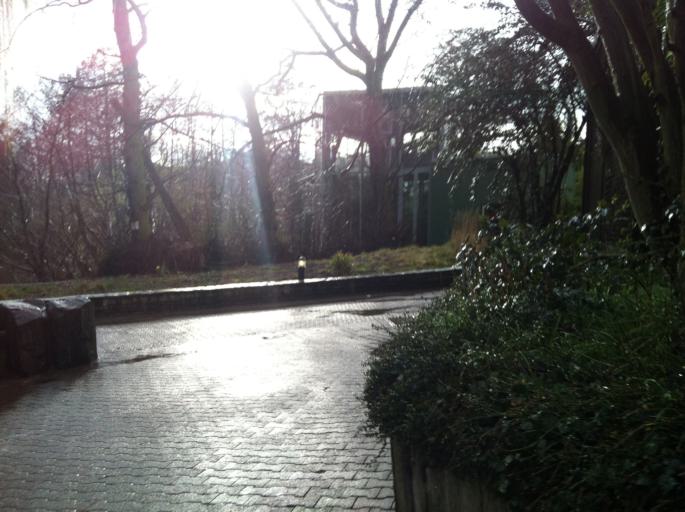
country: DE
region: Hesse
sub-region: Regierungsbezirk Darmstadt
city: Frankfurt am Main
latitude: 50.1162
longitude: 8.7023
